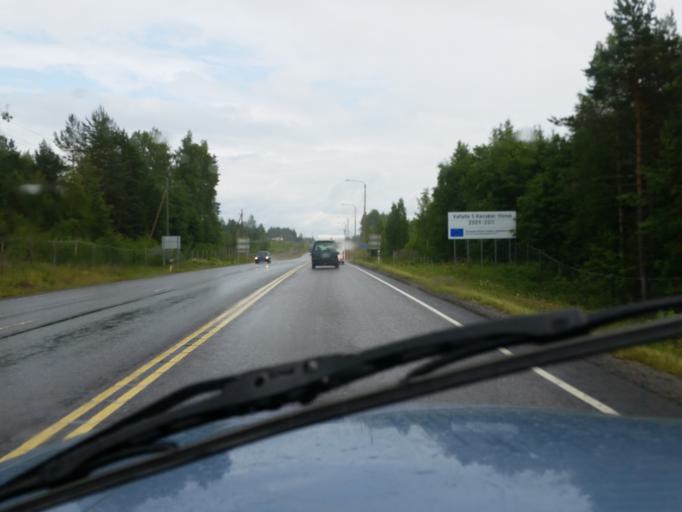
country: FI
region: Southern Savonia
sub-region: Mikkeli
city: Pertunmaa
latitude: 61.4356
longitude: 26.5480
